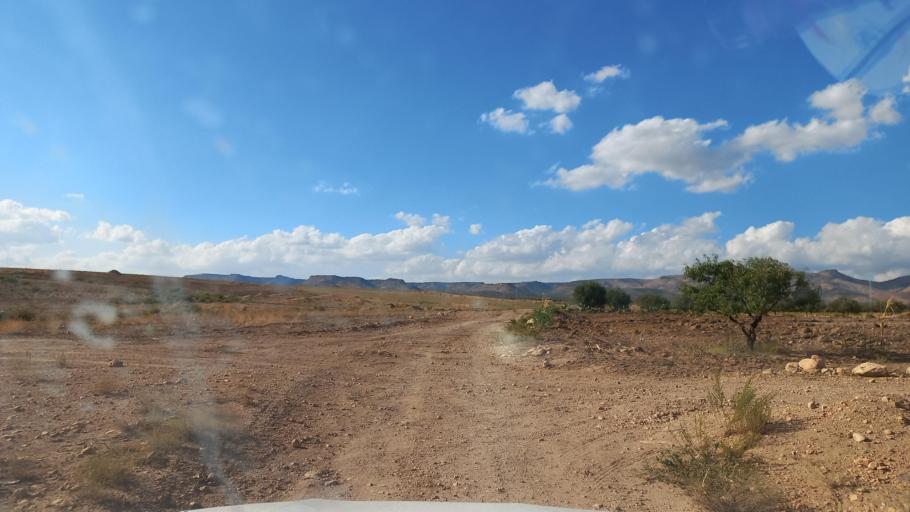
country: TN
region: Al Qasrayn
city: Sbiba
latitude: 35.3977
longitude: 9.0324
